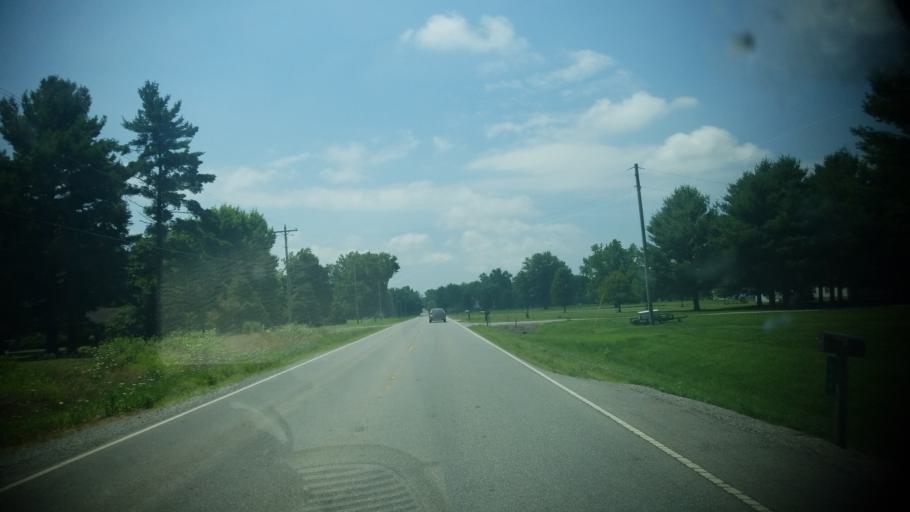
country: US
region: Illinois
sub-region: Wayne County
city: Fairfield
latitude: 38.3924
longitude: -88.3507
